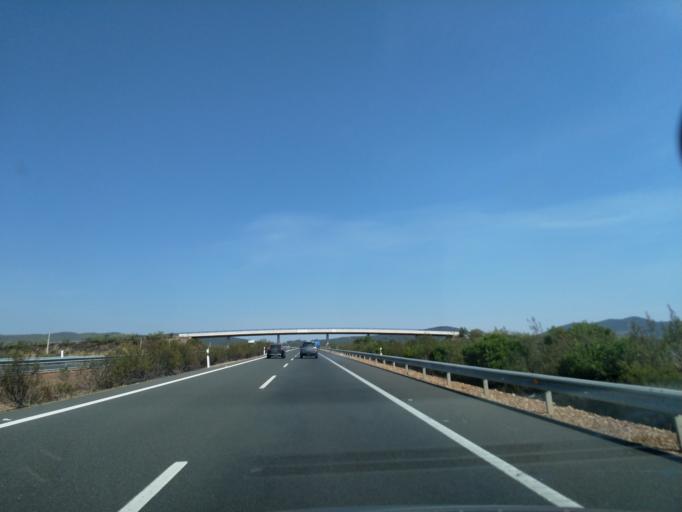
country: ES
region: Extremadura
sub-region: Provincia de Badajoz
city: Carmonita
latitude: 39.1278
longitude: -6.2763
